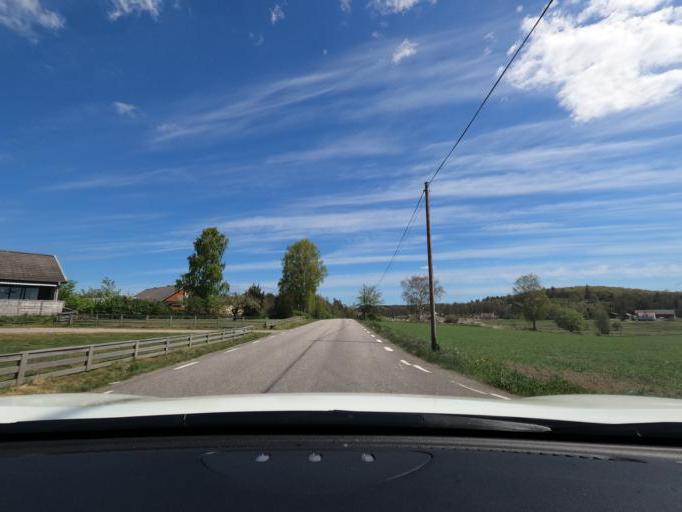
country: SE
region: Halland
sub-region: Kungsbacka Kommun
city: Fjaeras kyrkby
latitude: 57.3950
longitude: 12.2632
